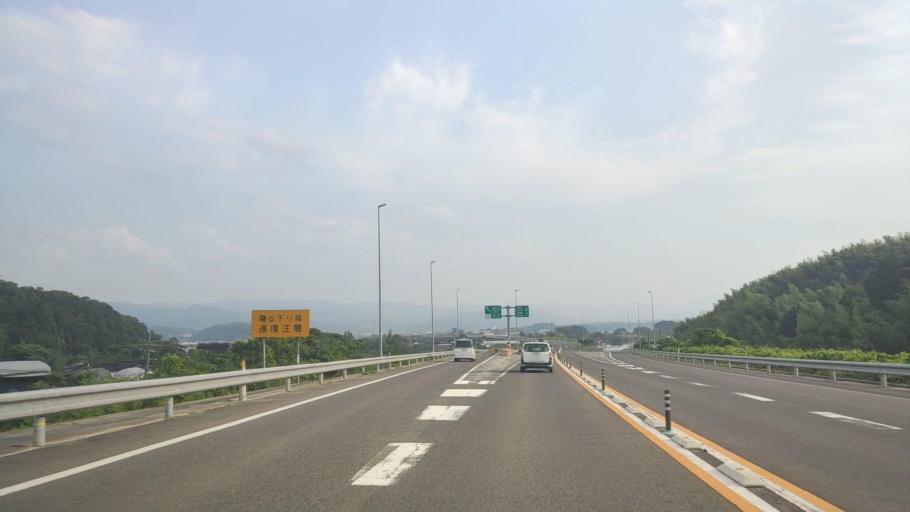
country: JP
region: Tottori
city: Kurayoshi
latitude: 35.4505
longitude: 133.8098
